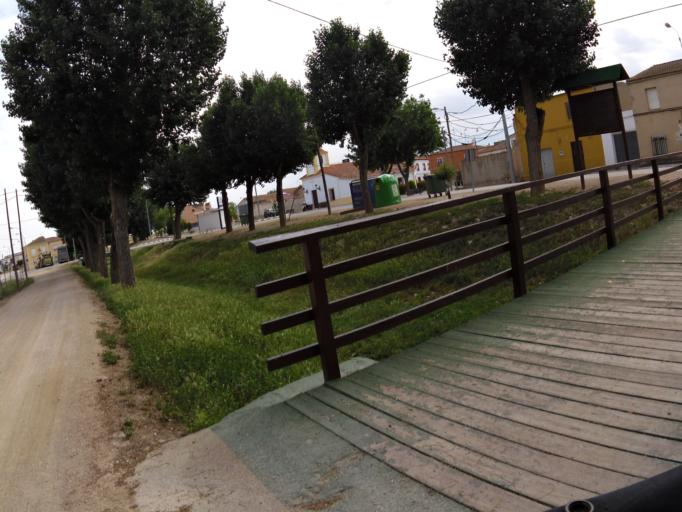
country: ES
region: Castille-La Mancha
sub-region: Provincia de Albacete
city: Valdeganga
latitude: 39.0683
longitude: -1.7441
